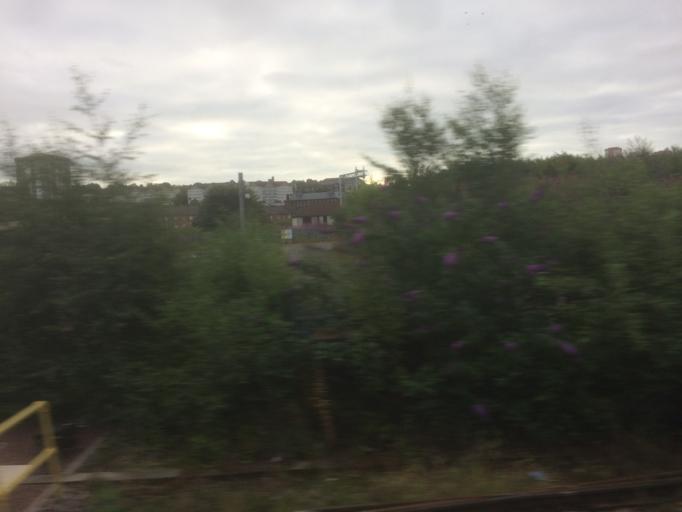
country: GB
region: Scotland
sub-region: Glasgow City
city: Glasgow
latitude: 55.8847
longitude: -4.2392
